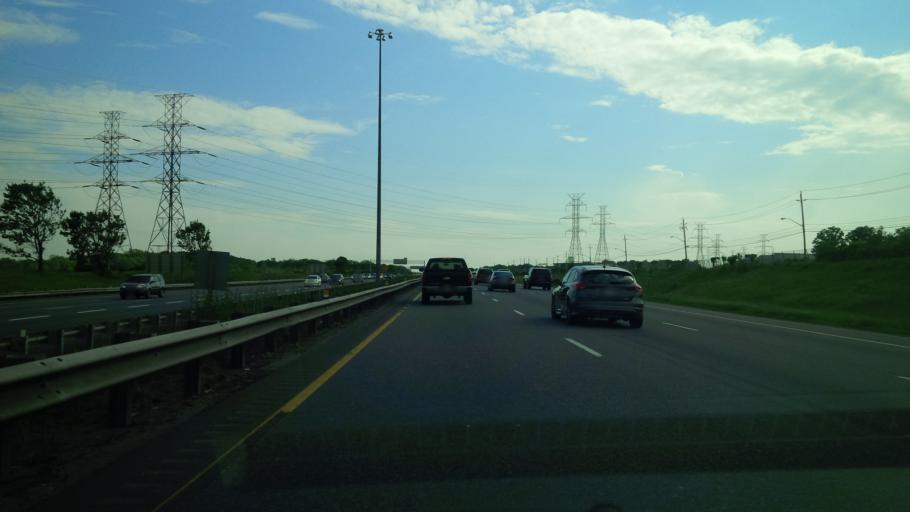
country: CA
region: Ontario
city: Burlington
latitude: 43.3279
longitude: -79.8436
